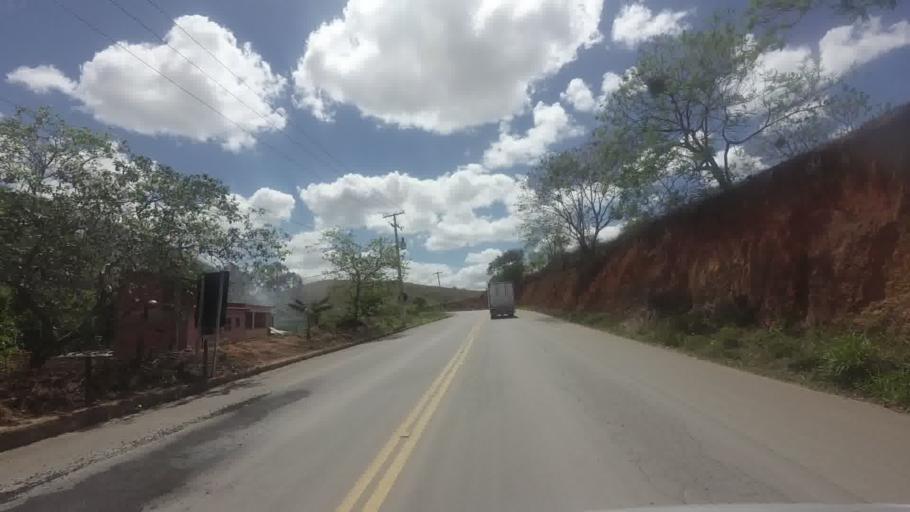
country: BR
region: Rio de Janeiro
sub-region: Santo Antonio De Padua
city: Santo Antonio de Padua
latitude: -21.6348
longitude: -42.2708
